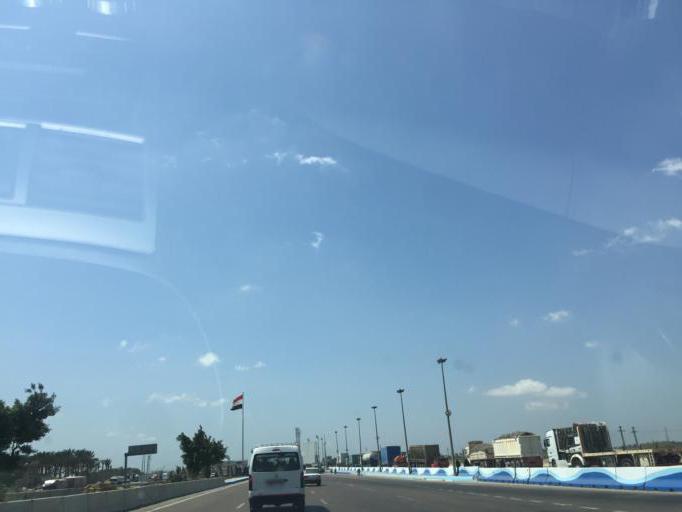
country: EG
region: Alexandria
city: Alexandria
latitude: 30.9662
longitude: 29.8306
